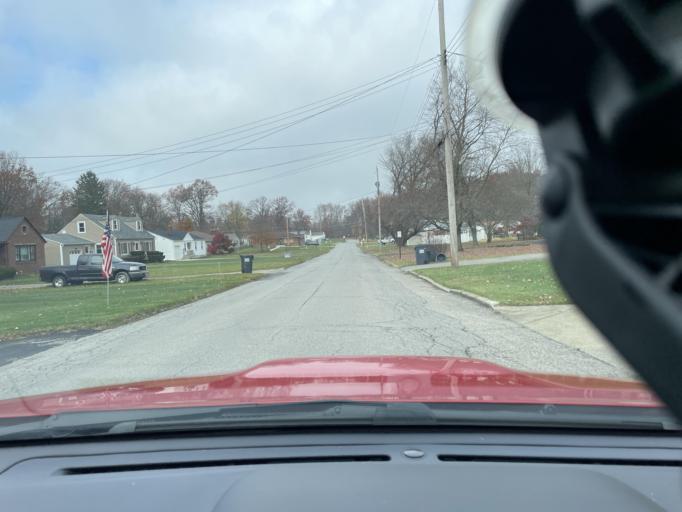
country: US
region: Ohio
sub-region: Mahoning County
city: Austintown
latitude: 41.1033
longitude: -80.7438
